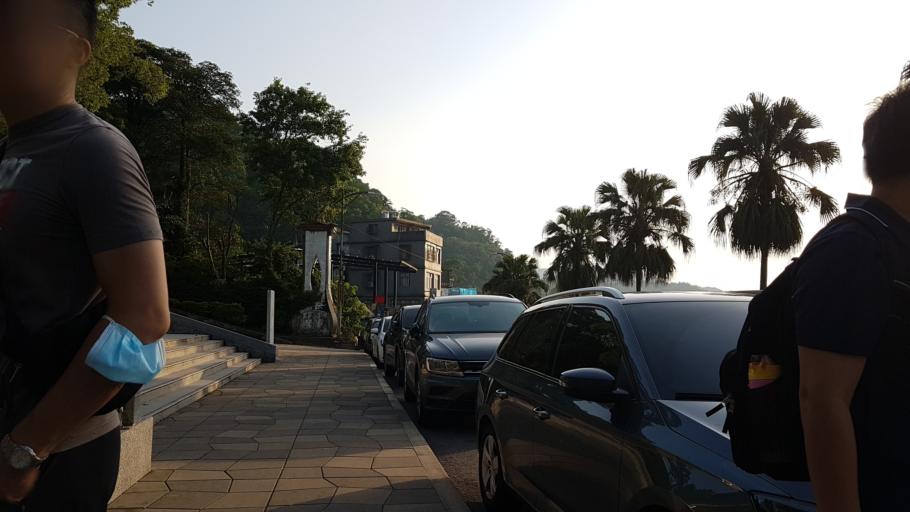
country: TW
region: Taiwan
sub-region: Yilan
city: Yilan
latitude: 24.9348
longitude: 121.7125
